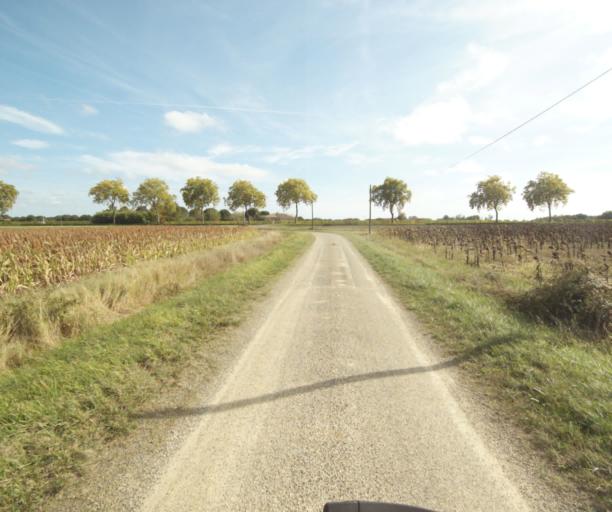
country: FR
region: Midi-Pyrenees
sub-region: Departement du Tarn-et-Garonne
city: Saint-Porquier
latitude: 43.9457
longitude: 1.1433
